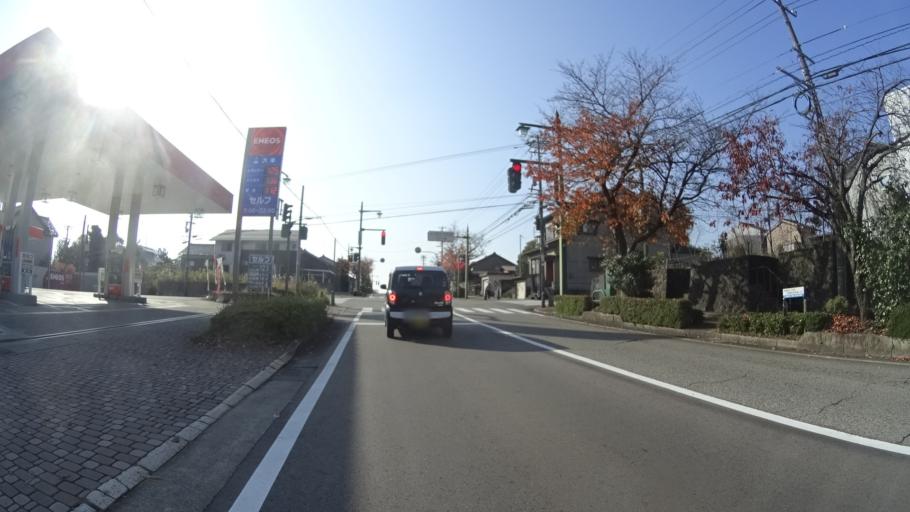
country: JP
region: Toyama
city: Nishishinminato
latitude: 36.7960
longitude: 137.0506
